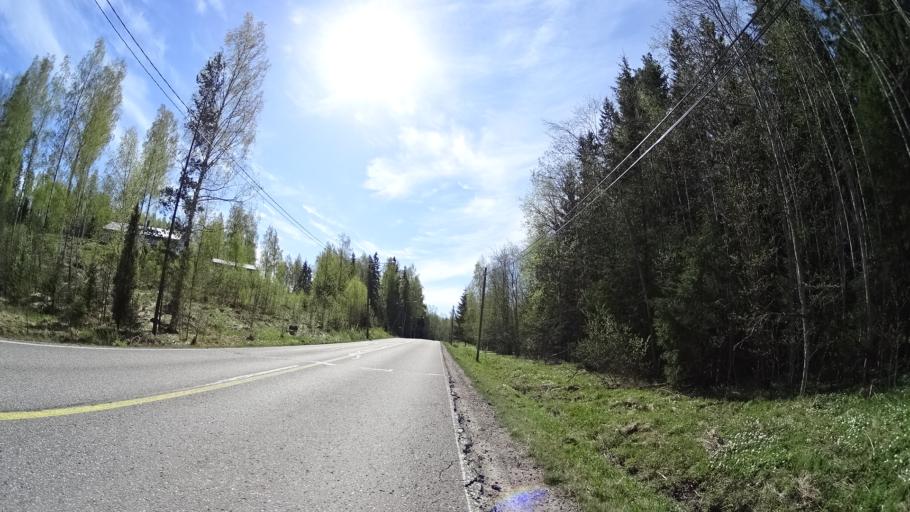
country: FI
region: Uusimaa
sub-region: Helsinki
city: Nurmijaervi
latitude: 60.3918
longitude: 24.8347
